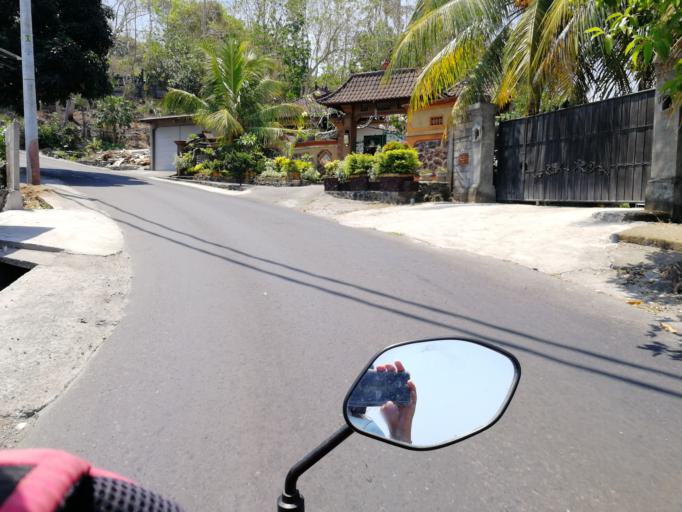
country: ID
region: Bali
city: Banjar Timbrah
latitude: -8.4750
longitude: 115.5959
